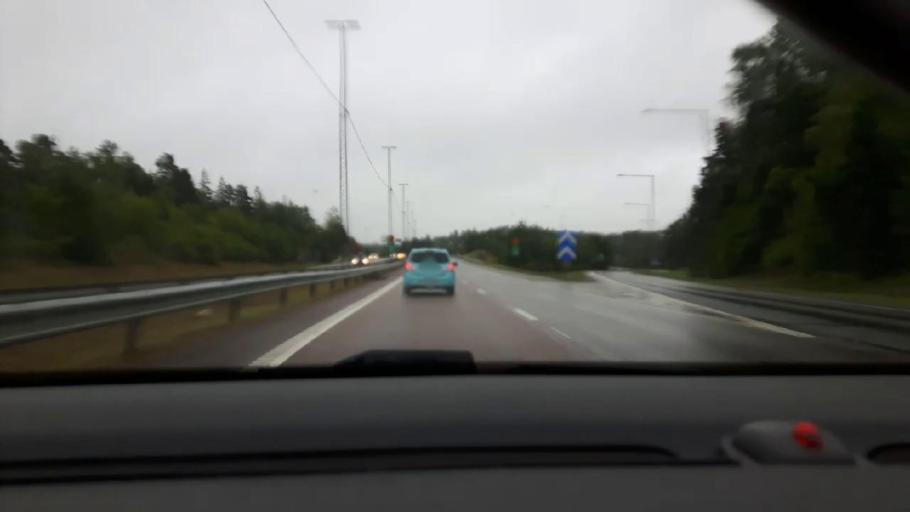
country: SE
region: Stockholm
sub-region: Sodertalje Kommun
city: Soedertaelje
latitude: 59.2021
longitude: 17.6539
